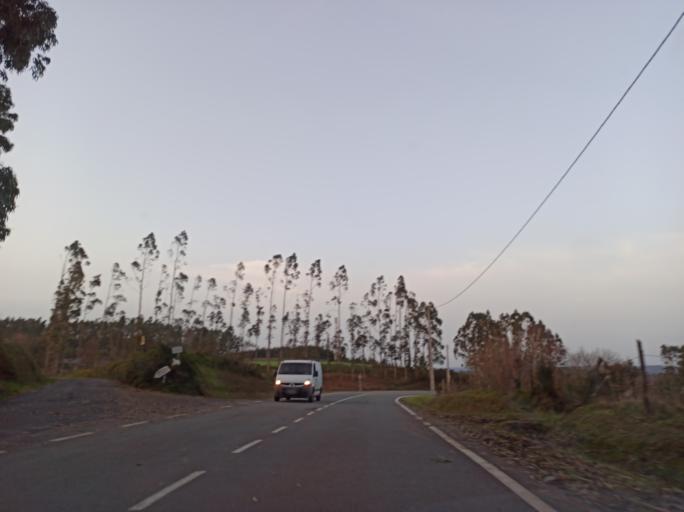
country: ES
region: Galicia
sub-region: Provincia da Coruna
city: Coiros
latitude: 43.1831
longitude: -8.1233
